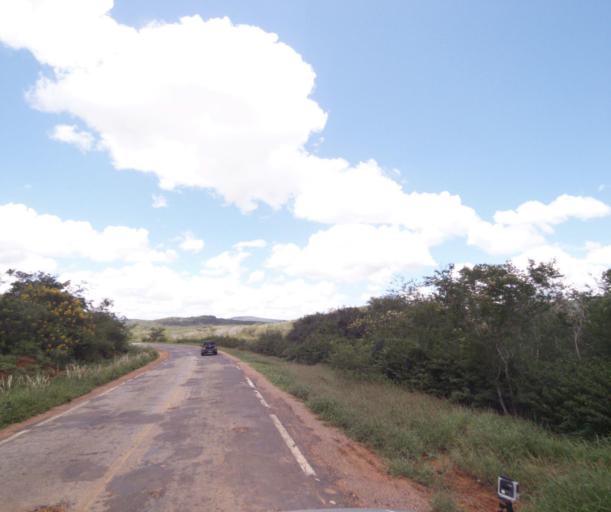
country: BR
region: Bahia
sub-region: Pocoes
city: Pocoes
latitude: -14.3865
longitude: -40.5184
